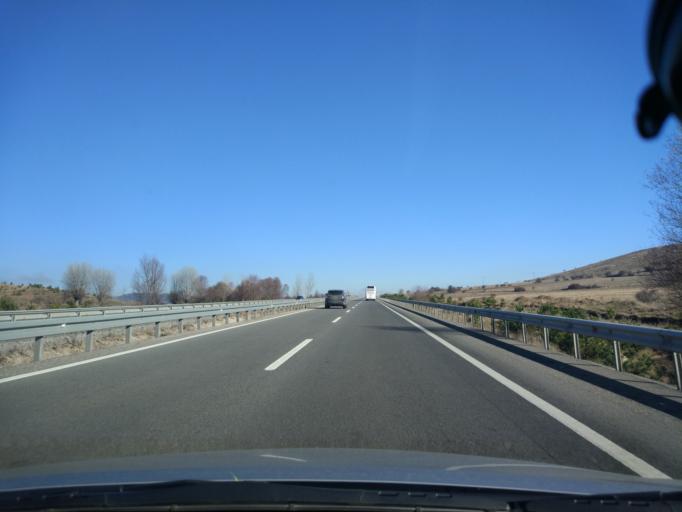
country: TR
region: Karabuk
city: Gozyeri
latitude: 40.8581
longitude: 32.4942
